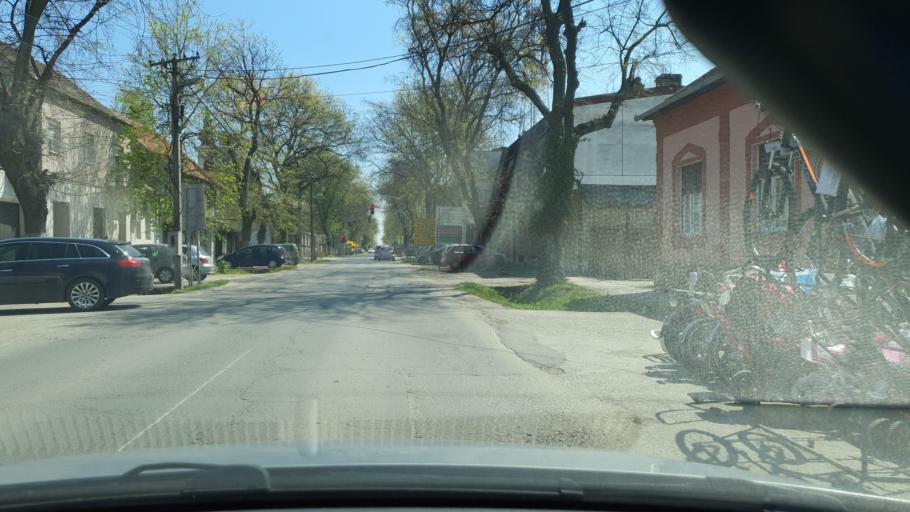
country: RS
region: Autonomna Pokrajina Vojvodina
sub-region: Zapadnobacki Okrug
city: Odzaci
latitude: 45.5077
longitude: 19.2573
